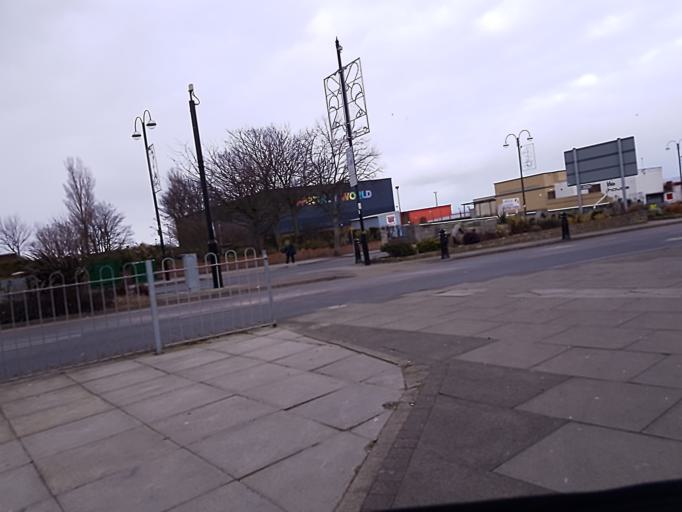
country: GB
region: England
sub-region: North East Lincolnshire
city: Cleethorpes
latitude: 53.5605
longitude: -0.0286
